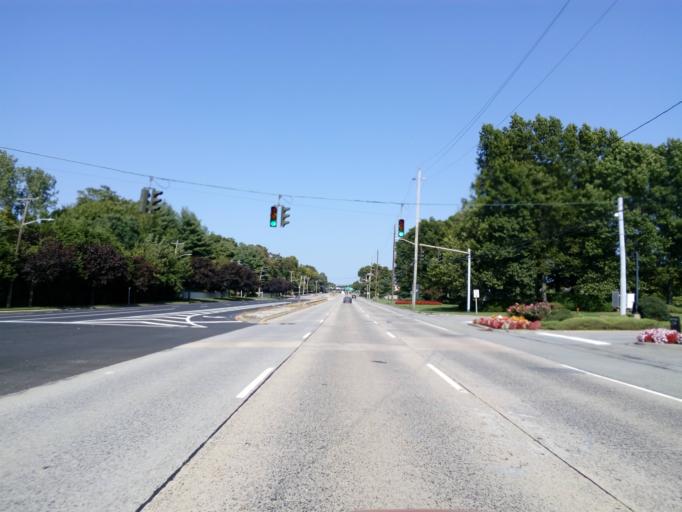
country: US
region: New York
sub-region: Nassau County
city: Jericho
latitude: 40.7867
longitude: -73.5487
